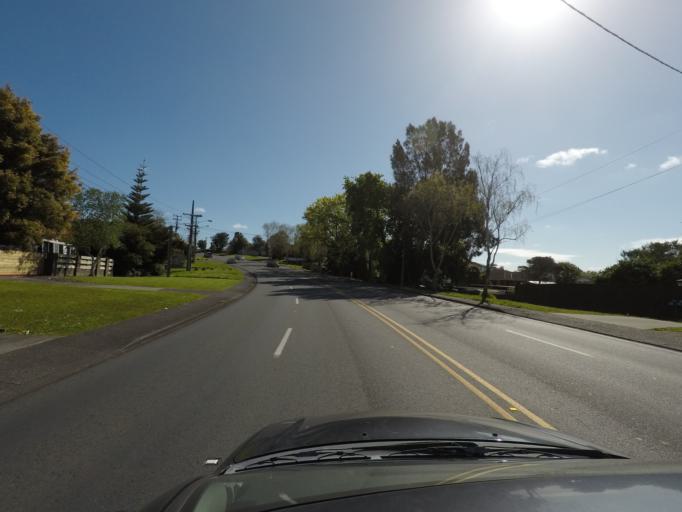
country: NZ
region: Auckland
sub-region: Auckland
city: Rosebank
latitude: -36.8608
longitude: 174.6105
